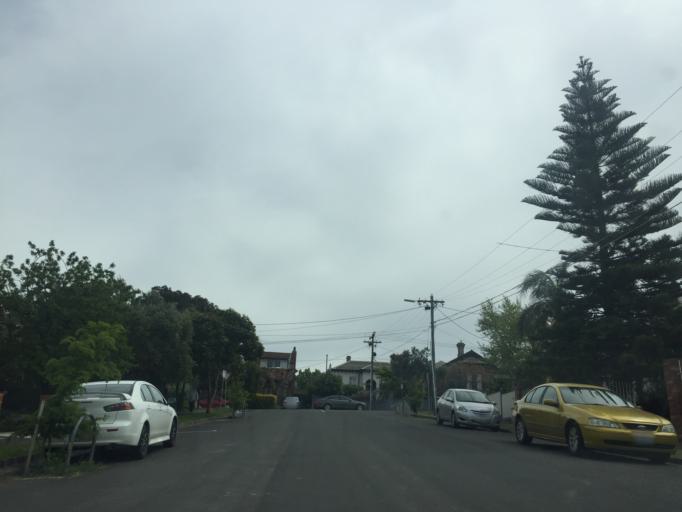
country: AU
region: Victoria
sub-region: Darebin
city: Northcote
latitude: -37.7733
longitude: 145.0012
